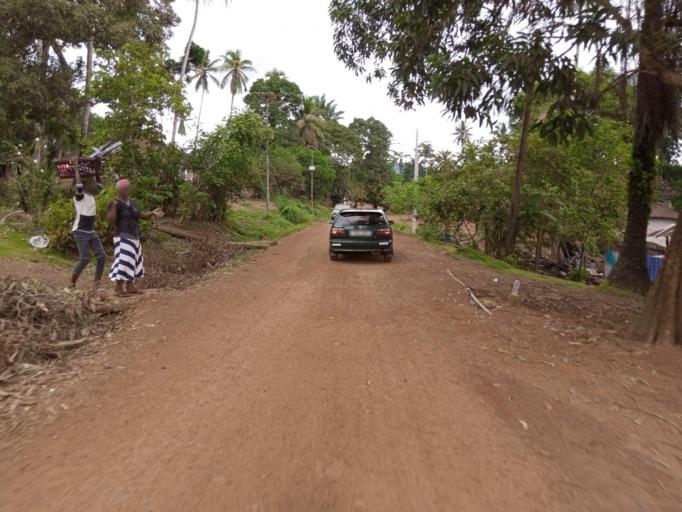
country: SL
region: Southern Province
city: Moyamba
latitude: 8.1649
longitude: -12.4279
